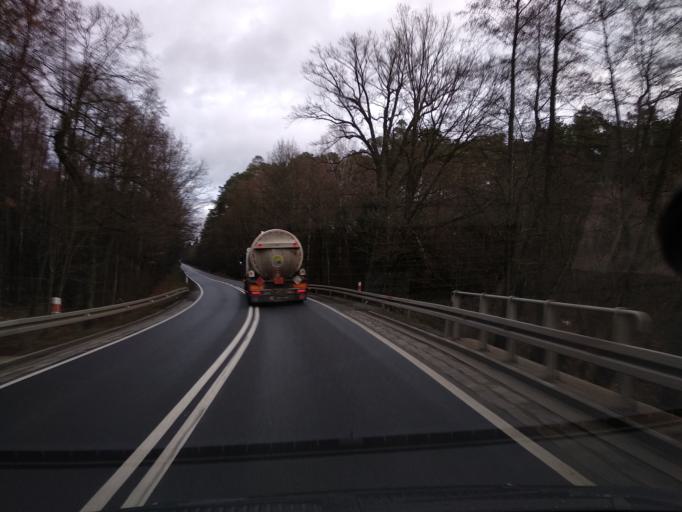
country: PL
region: Lower Silesian Voivodeship
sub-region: Powiat olesnicki
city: Miedzyborz
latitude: 51.3518
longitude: 17.6027
